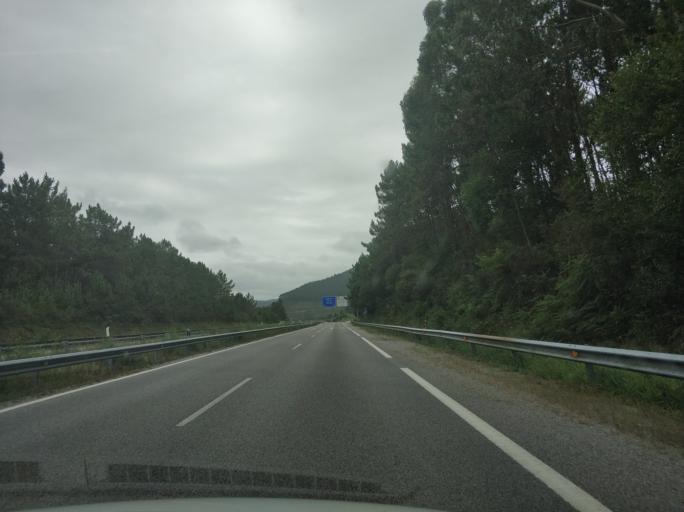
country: ES
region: Asturias
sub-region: Province of Asturias
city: Cudillero
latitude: 43.5616
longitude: -6.2112
